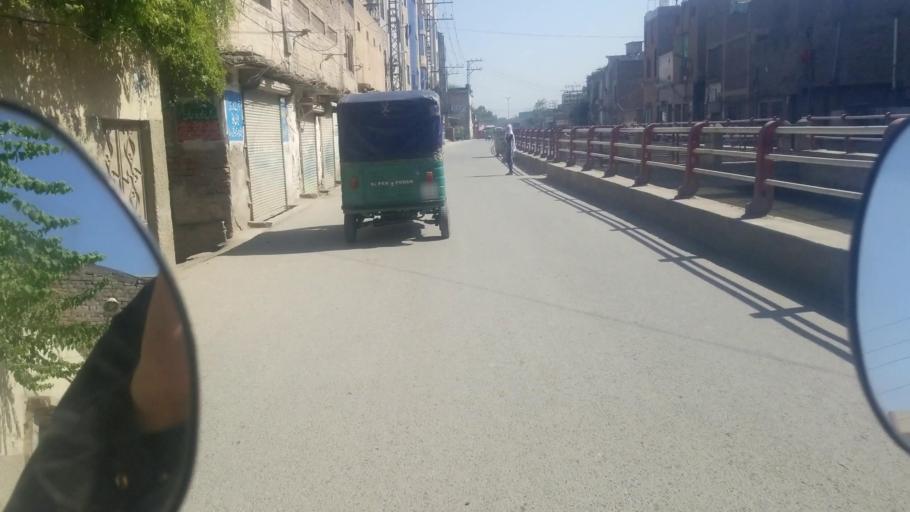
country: PK
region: Khyber Pakhtunkhwa
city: Peshawar
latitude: 34.0205
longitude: 71.5926
